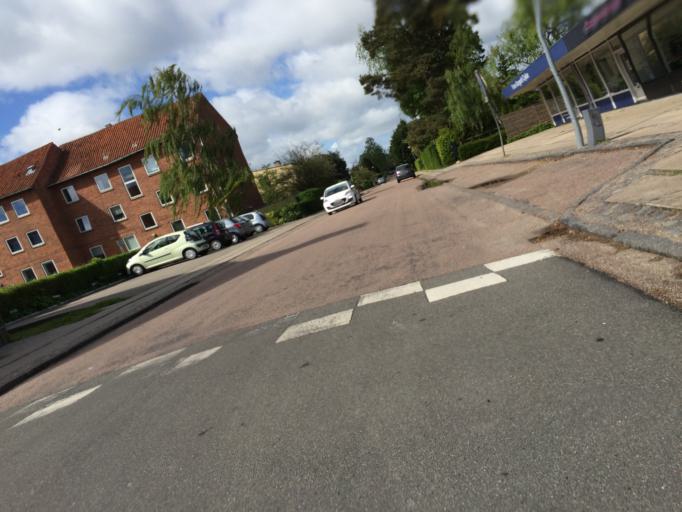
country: DK
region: Capital Region
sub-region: Rudersdal Kommune
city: Holte
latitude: 55.7958
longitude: 12.4690
